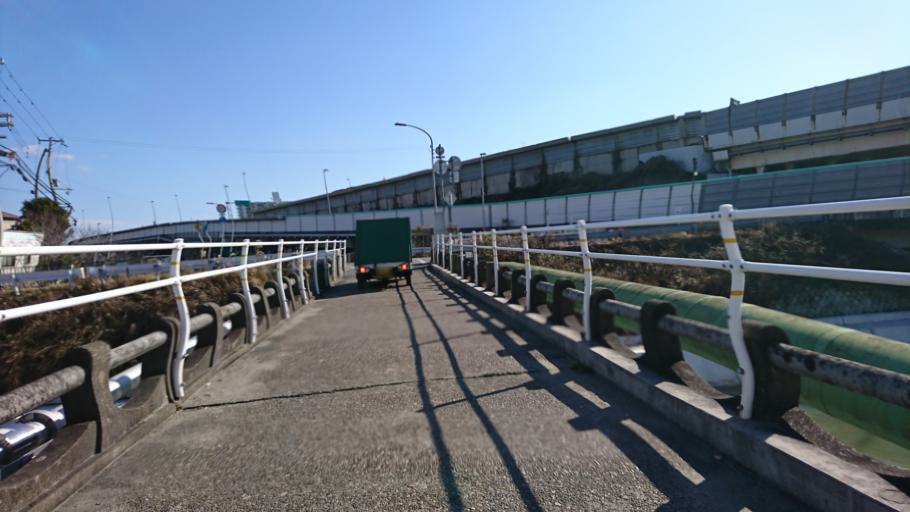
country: JP
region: Hyogo
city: Kakogawacho-honmachi
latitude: 34.7917
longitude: 134.7999
